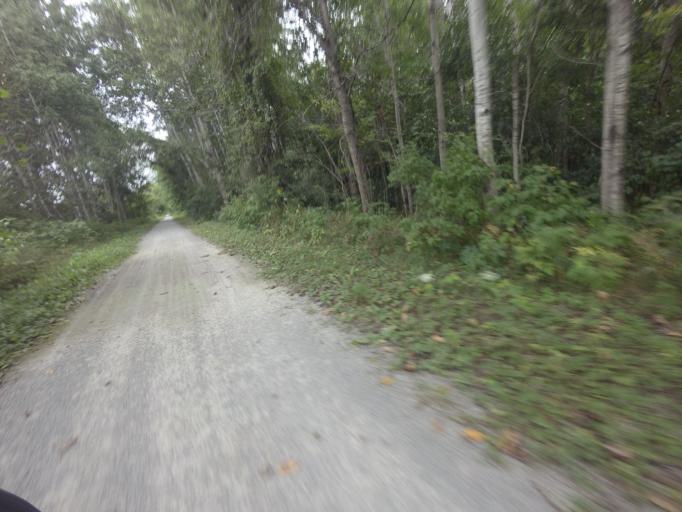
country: CA
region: Ontario
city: Omemee
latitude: 44.3314
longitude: -78.7651
